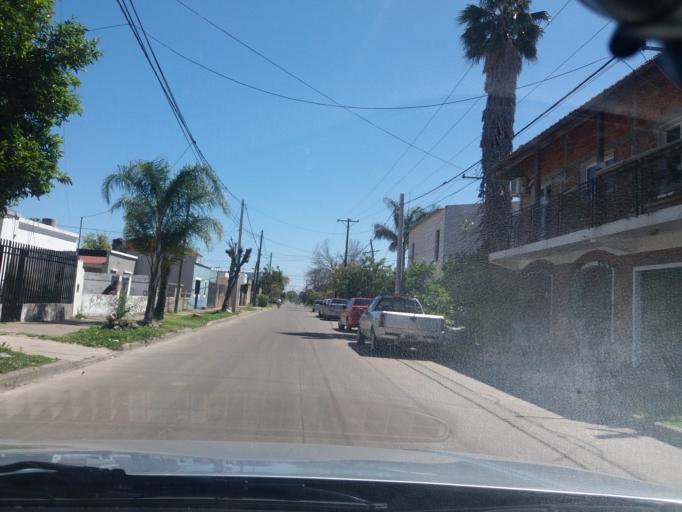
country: AR
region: Corrientes
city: Corrientes
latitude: -27.4895
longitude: -58.8353
